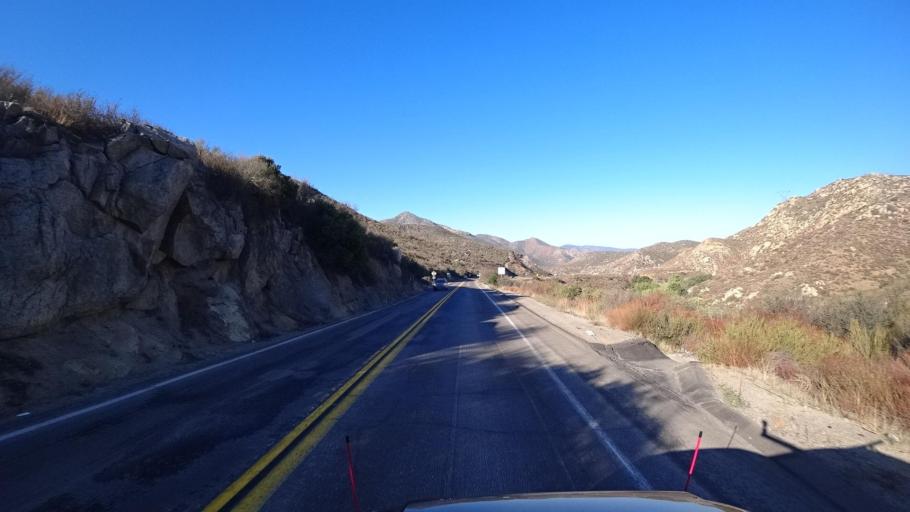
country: MX
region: Baja California
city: Tecate
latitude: 32.5978
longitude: -116.6440
